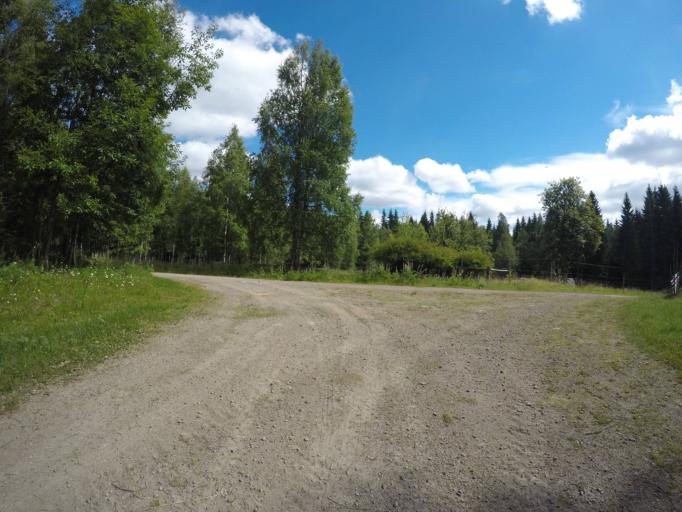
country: SE
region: OErebro
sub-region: Hallefors Kommun
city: Haellefors
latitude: 60.0678
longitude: 14.4625
